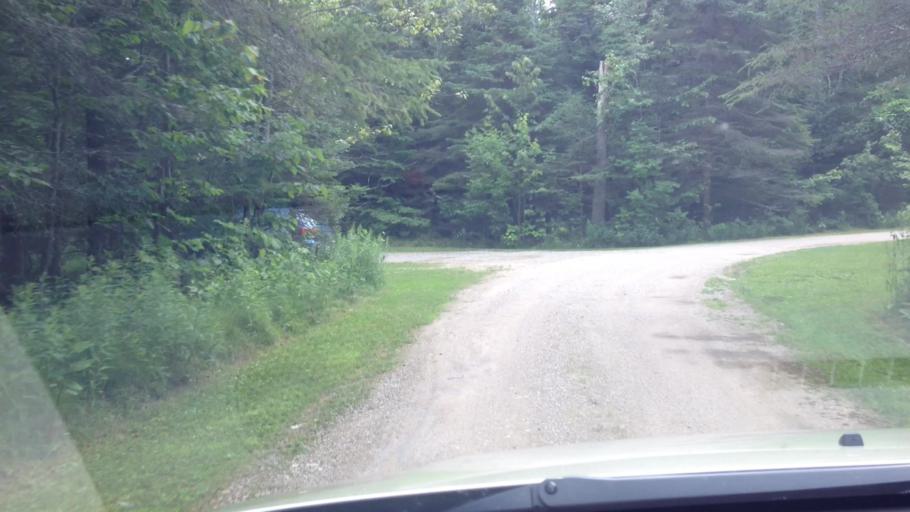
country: US
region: Michigan
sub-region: Menominee County
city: Menominee
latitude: 45.4014
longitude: -87.3604
